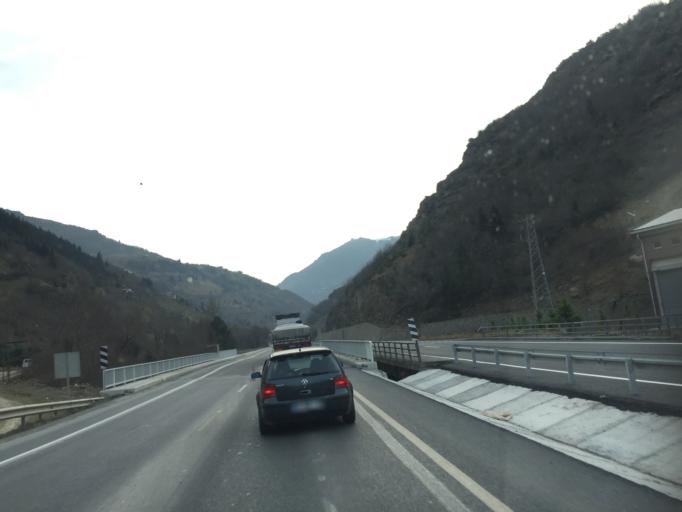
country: TR
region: Trabzon
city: Macka
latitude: 40.7961
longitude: 39.5841
